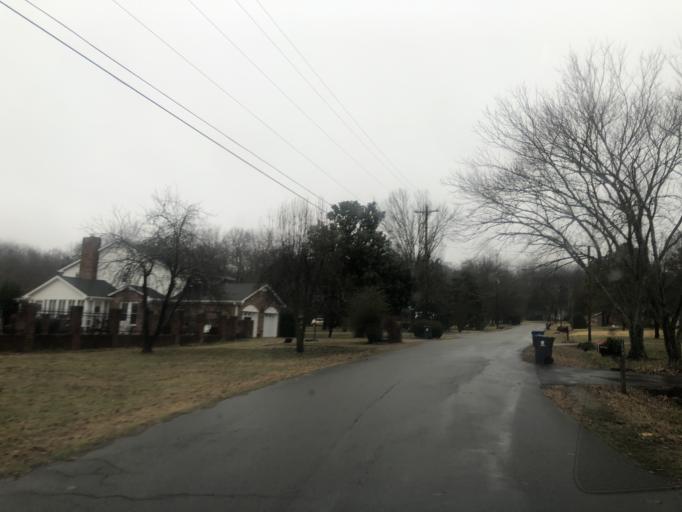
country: US
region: Tennessee
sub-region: Davidson County
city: Belle Meade
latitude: 36.0853
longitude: -86.9504
